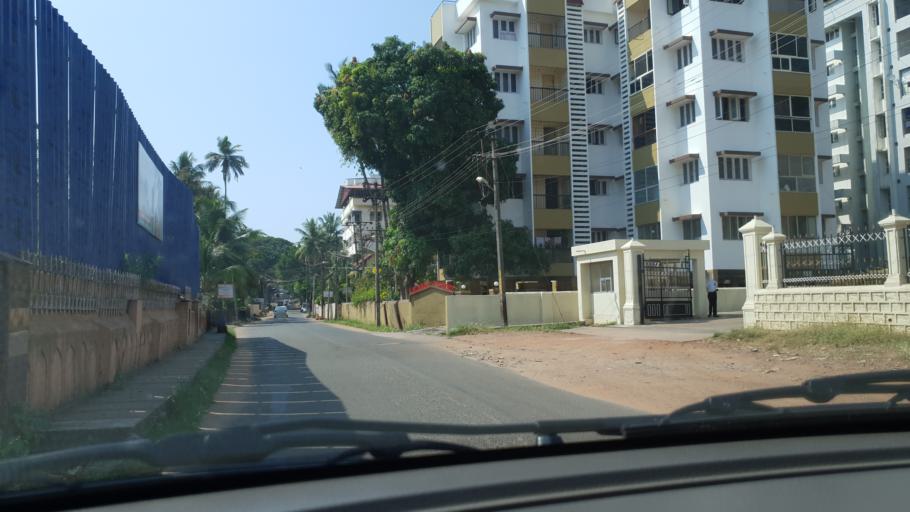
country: IN
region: Karnataka
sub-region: Dakshina Kannada
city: Mangalore
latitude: 12.8842
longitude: 74.8384
